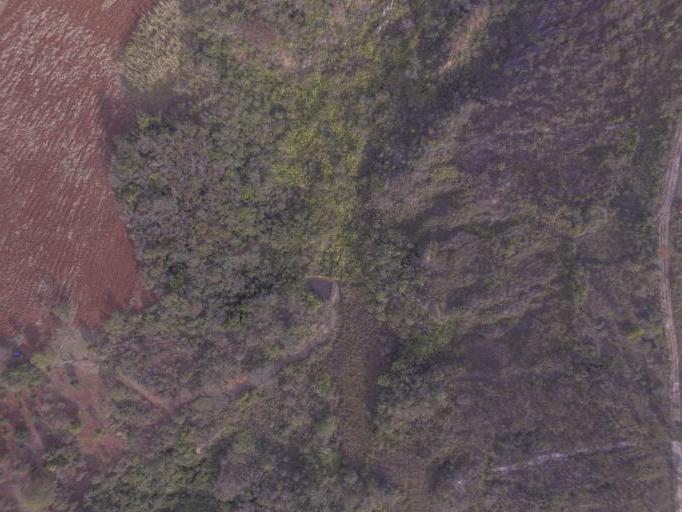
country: BR
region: Minas Gerais
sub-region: Tiradentes
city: Tiradentes
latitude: -21.0562
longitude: -44.1031
